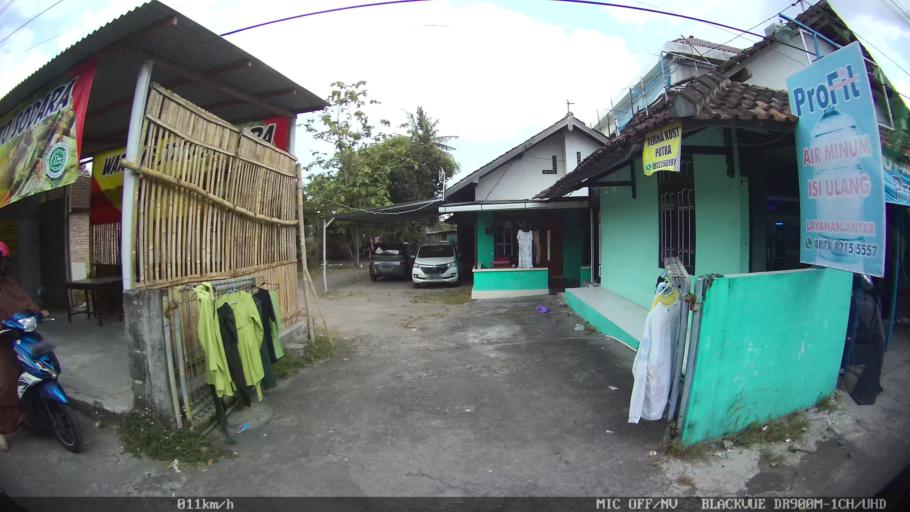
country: ID
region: Daerah Istimewa Yogyakarta
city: Gamping Lor
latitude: -7.8073
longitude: 110.3276
